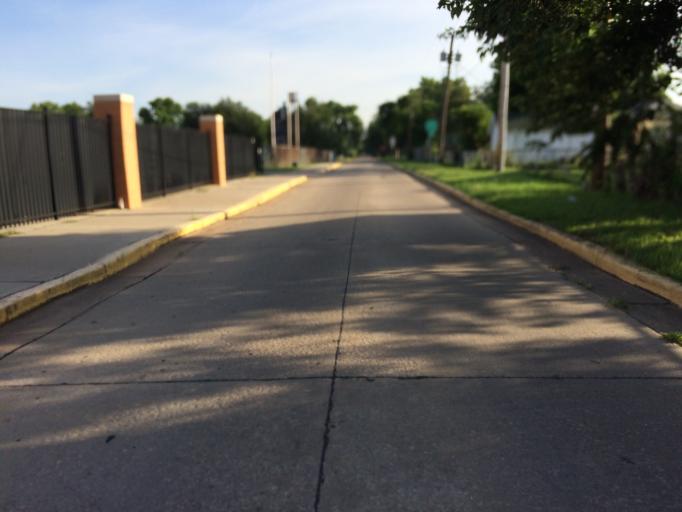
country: US
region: Oklahoma
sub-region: Cleveland County
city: Norman
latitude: 35.2209
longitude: -97.4546
